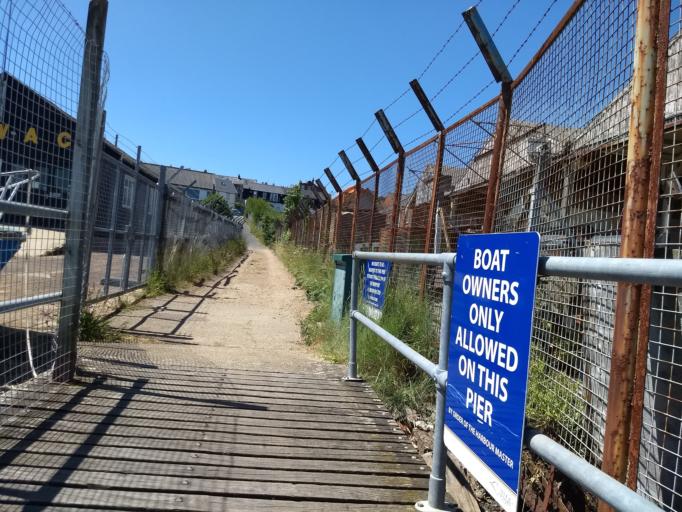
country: GB
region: England
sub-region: Isle of Wight
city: East Cowes
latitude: 50.7538
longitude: -1.2944
